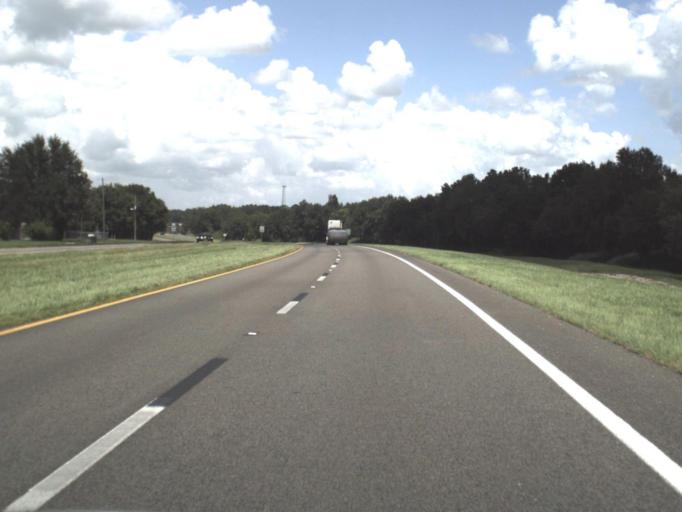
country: US
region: Florida
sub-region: Polk County
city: Fort Meade
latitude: 27.7759
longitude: -81.8016
